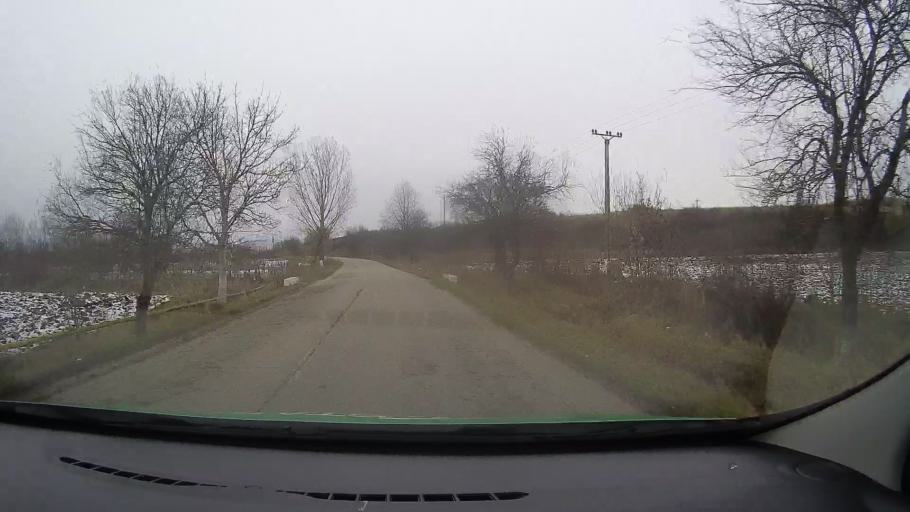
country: RO
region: Hunedoara
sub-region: Comuna Romos
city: Romos
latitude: 45.8645
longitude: 23.2738
